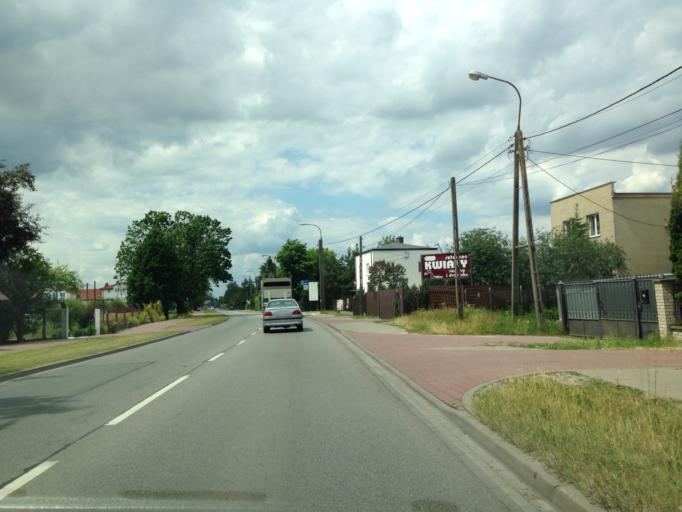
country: PL
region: Masovian Voivodeship
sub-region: Warszawa
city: Bemowo
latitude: 52.2412
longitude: 20.8807
